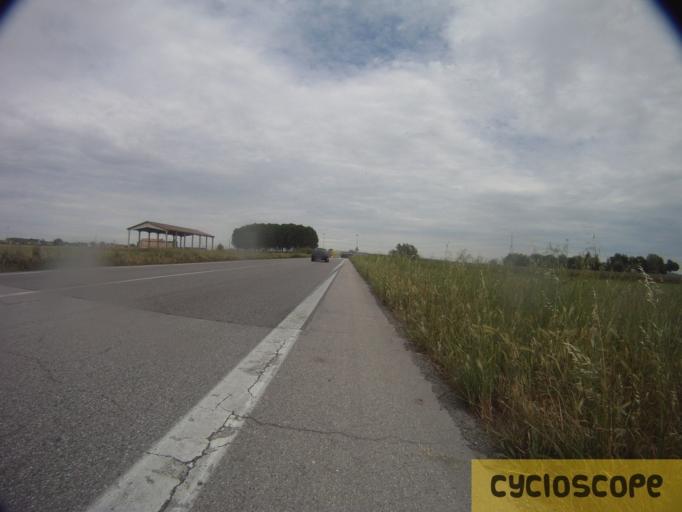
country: IT
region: Veneto
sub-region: Provincia di Rovigo
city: Taglio di Po
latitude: 44.9759
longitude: 12.2217
